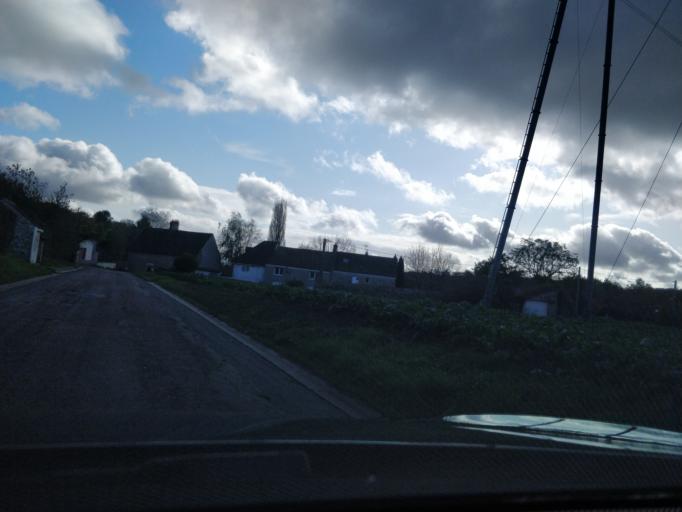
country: FR
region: Ile-de-France
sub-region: Departement de l'Essonne
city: Fontenay-les-Briis
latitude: 48.6353
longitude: 2.1558
